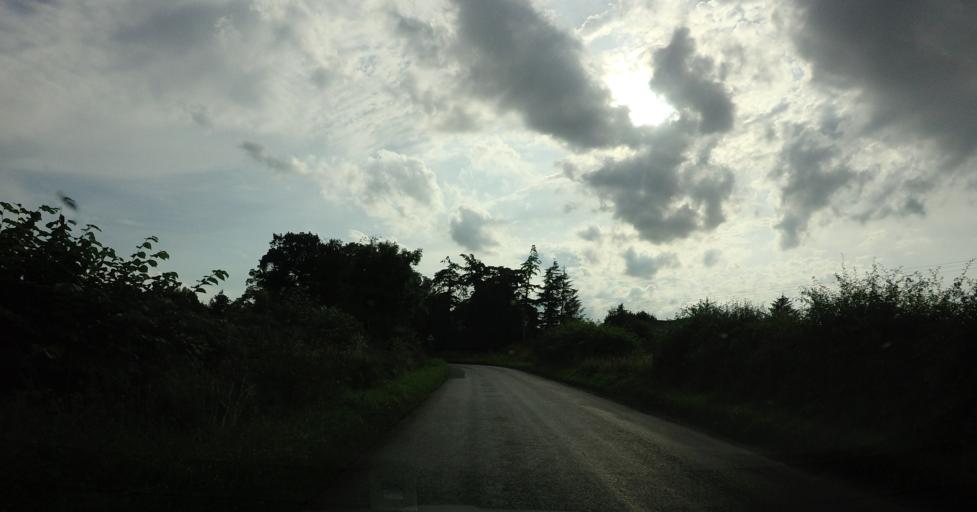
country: GB
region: Scotland
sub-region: Perth and Kinross
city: Auchterarder
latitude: 56.3028
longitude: -3.7482
